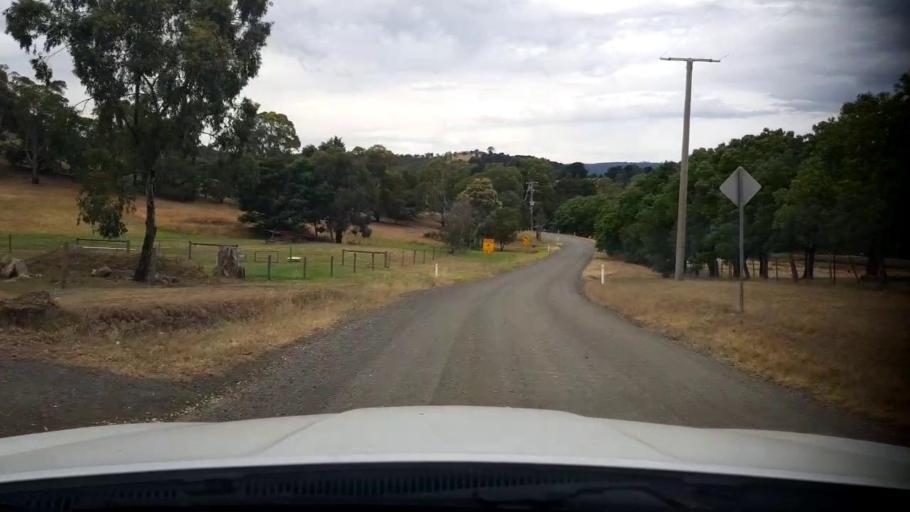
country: AU
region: Victoria
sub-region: Whittlesea
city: Whittlesea
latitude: -37.4917
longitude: 145.0628
